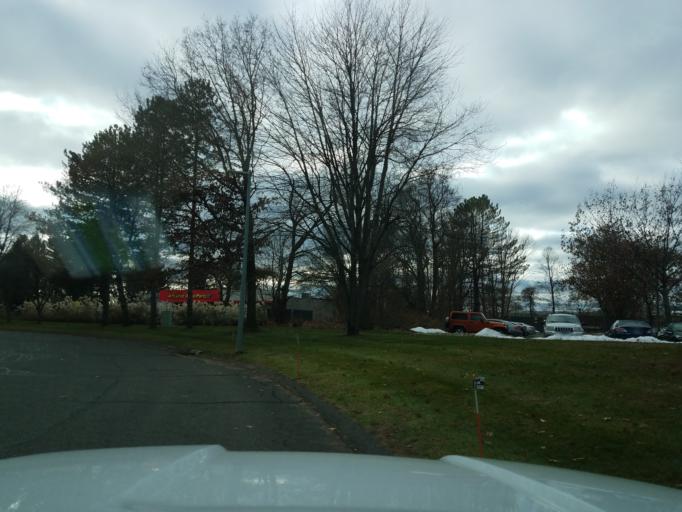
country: US
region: Connecticut
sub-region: Hartford County
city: Windsor Locks
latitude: 41.9306
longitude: -72.6106
